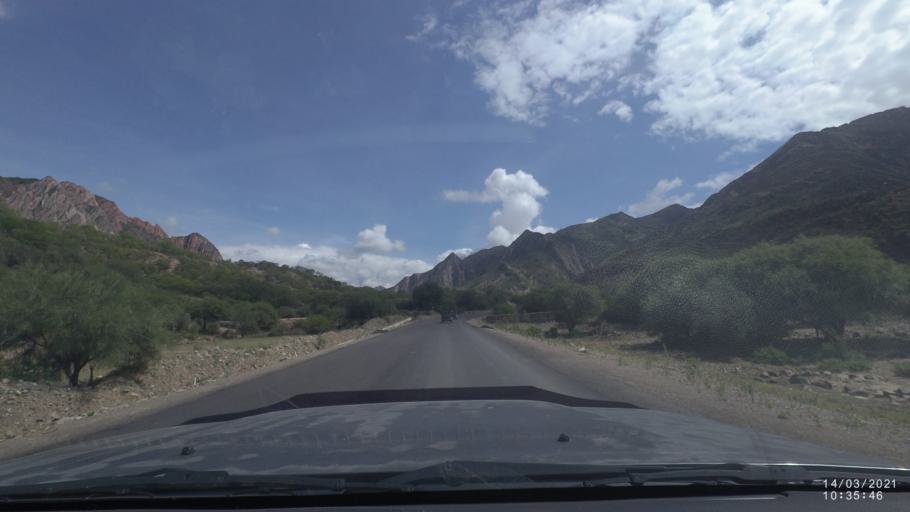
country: BO
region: Cochabamba
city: Cliza
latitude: -17.9068
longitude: -65.8805
